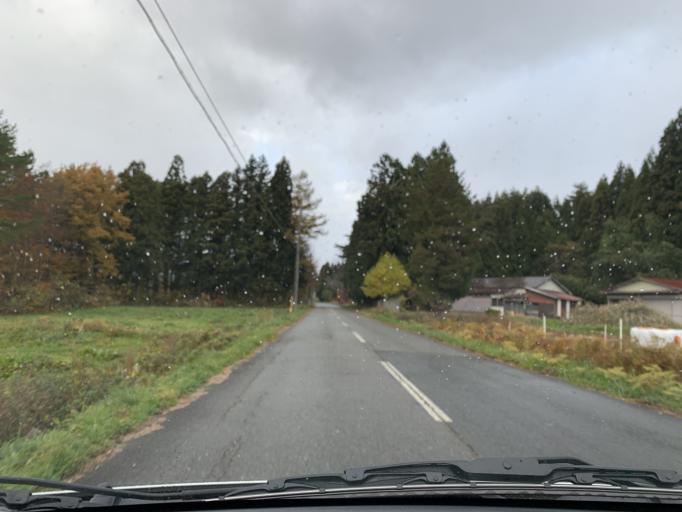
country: JP
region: Iwate
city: Mizusawa
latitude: 39.0926
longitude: 140.9941
